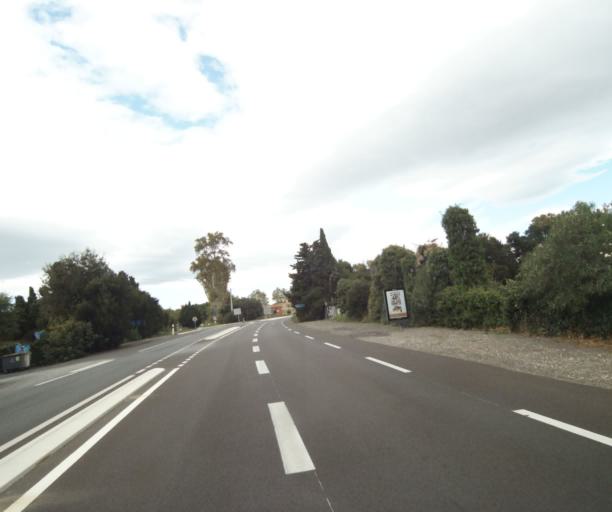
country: FR
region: Languedoc-Roussillon
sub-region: Departement des Pyrenees-Orientales
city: Elne
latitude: 42.5921
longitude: 2.9789
